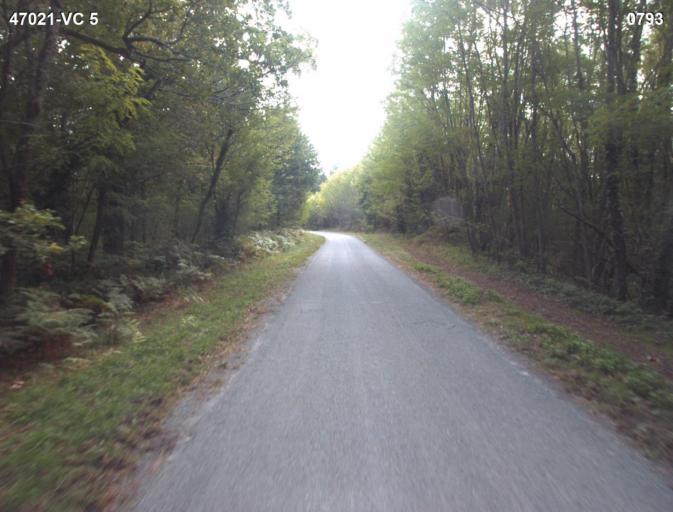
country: FR
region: Aquitaine
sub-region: Departement du Lot-et-Garonne
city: Barbaste
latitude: 44.1427
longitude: 0.2864
